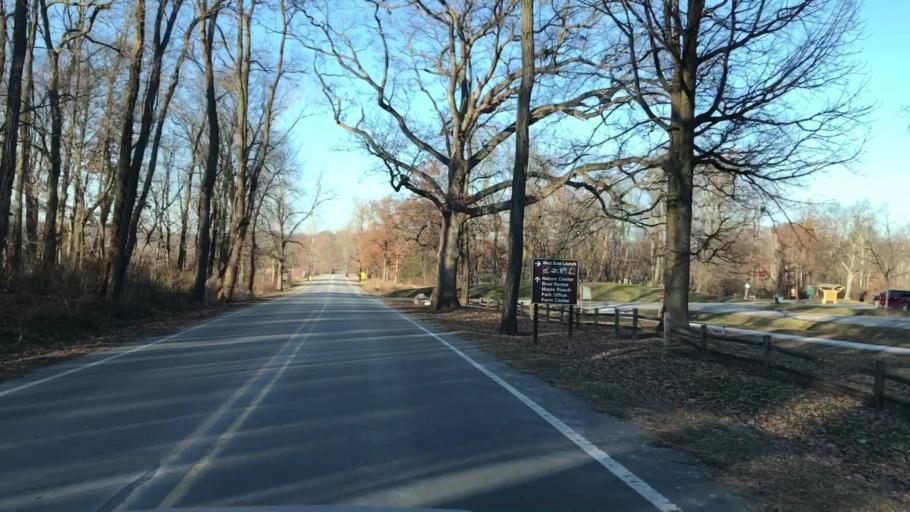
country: US
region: Michigan
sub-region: Oakland County
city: South Lyon
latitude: 42.5241
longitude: -83.6711
